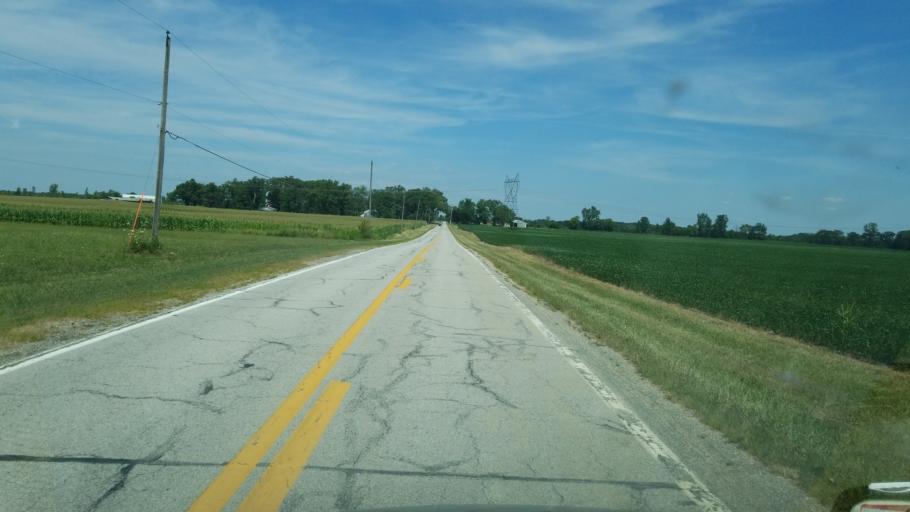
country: US
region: Ohio
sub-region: Madison County
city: Mount Sterling
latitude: 39.8302
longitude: -83.2363
